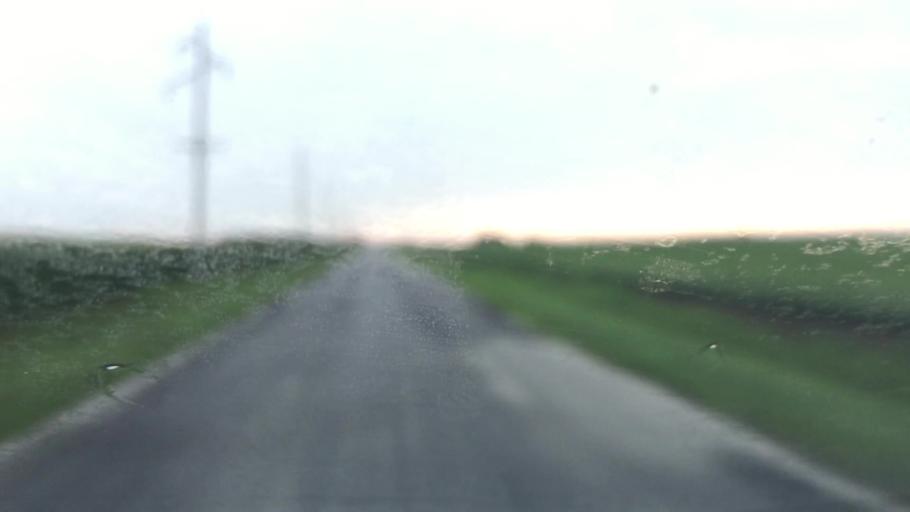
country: US
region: Iowa
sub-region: Lee County
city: Fort Madison
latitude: 40.5551
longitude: -91.2687
